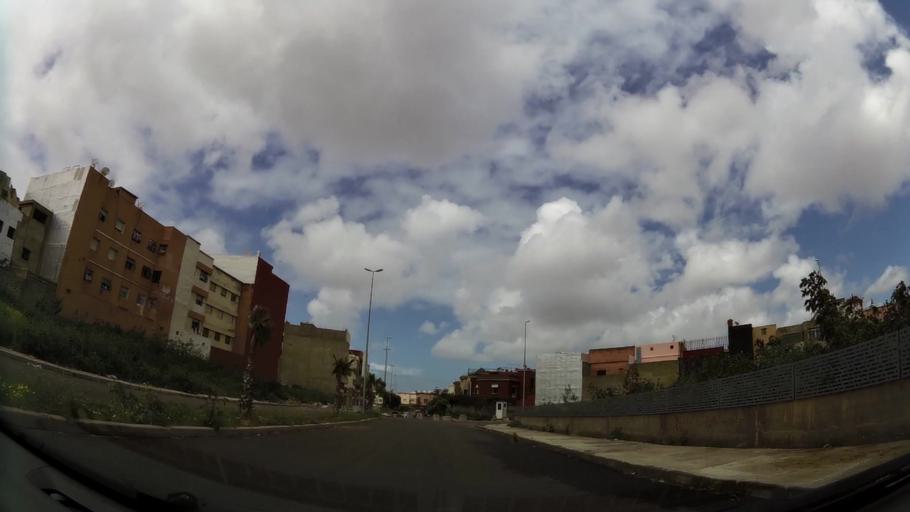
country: MA
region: Grand Casablanca
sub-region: Casablanca
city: Casablanca
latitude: 33.5312
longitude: -7.6044
